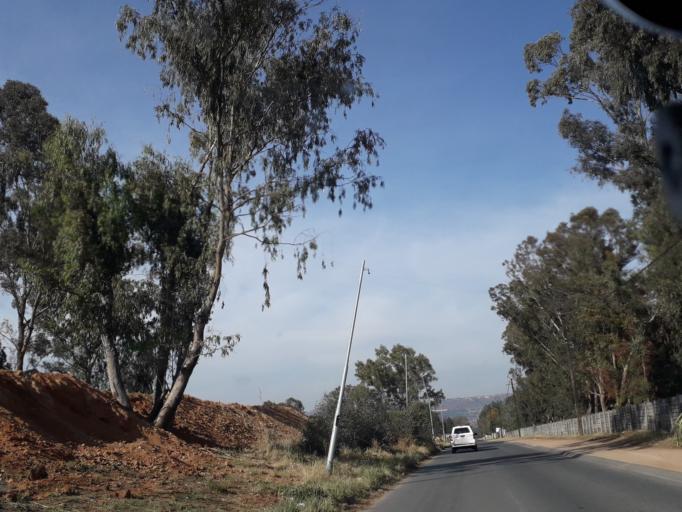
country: ZA
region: Gauteng
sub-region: West Rand District Municipality
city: Muldersdriseloop
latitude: -26.0651
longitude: 27.9036
